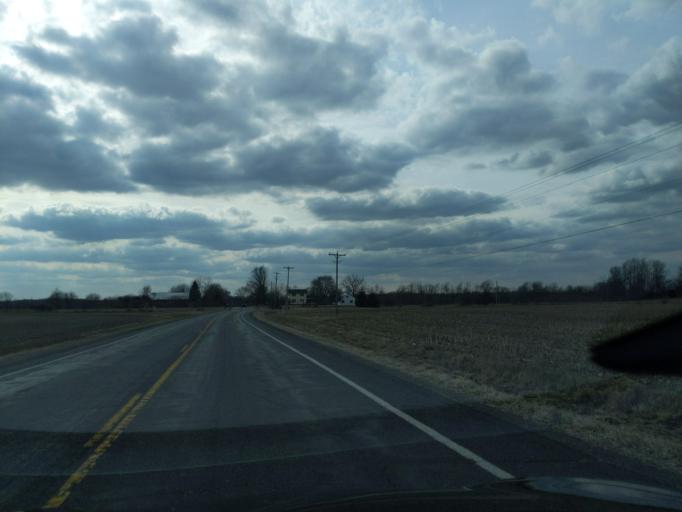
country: US
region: Michigan
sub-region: Ingham County
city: Mason
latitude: 42.5240
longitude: -84.4811
